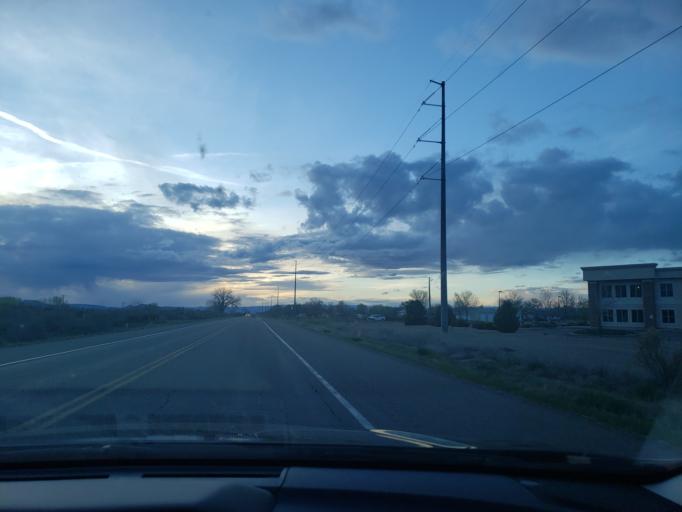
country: US
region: Colorado
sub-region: Mesa County
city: Fruita
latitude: 39.1338
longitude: -108.6910
